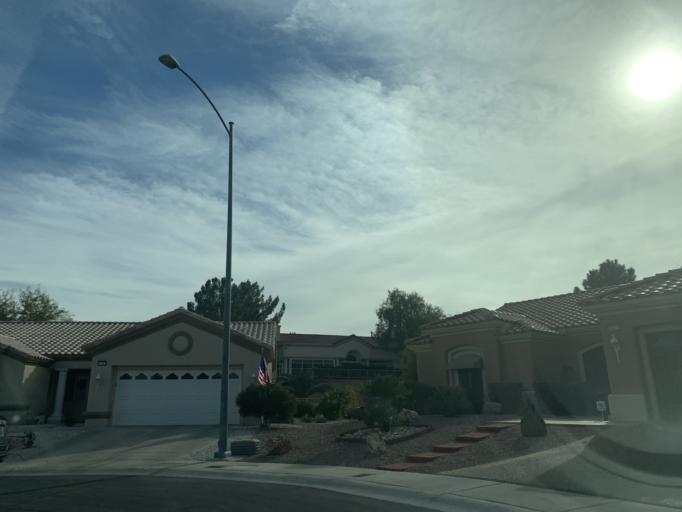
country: US
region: Nevada
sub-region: Clark County
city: Summerlin South
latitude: 36.2176
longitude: -115.3242
